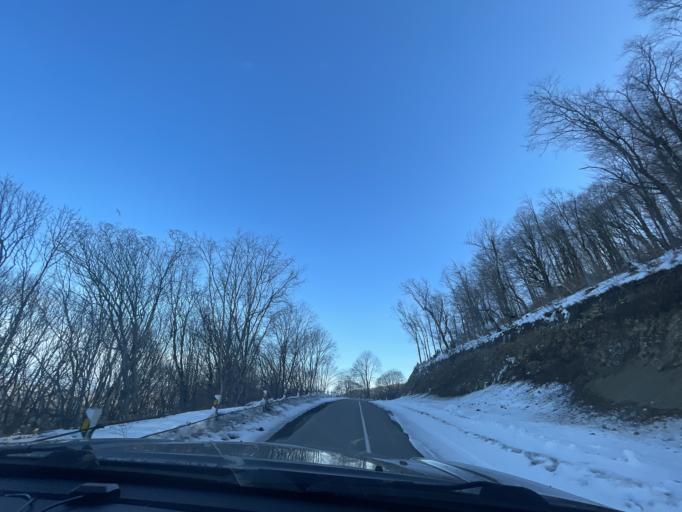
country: GE
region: Kvemo Kartli
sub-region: Tetri Tsqaro
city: Manglisi
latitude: 41.7705
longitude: 44.5066
